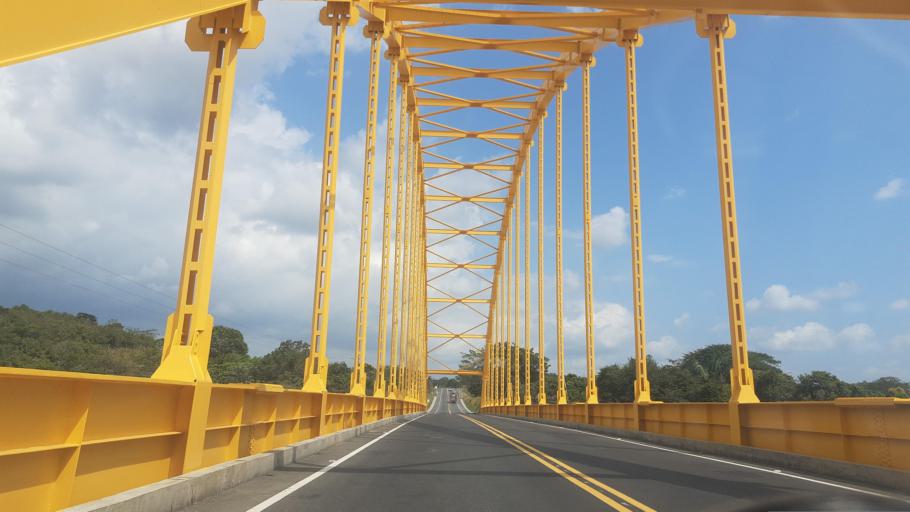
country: CO
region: Casanare
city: Tauramena
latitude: 4.9268
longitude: -72.6728
